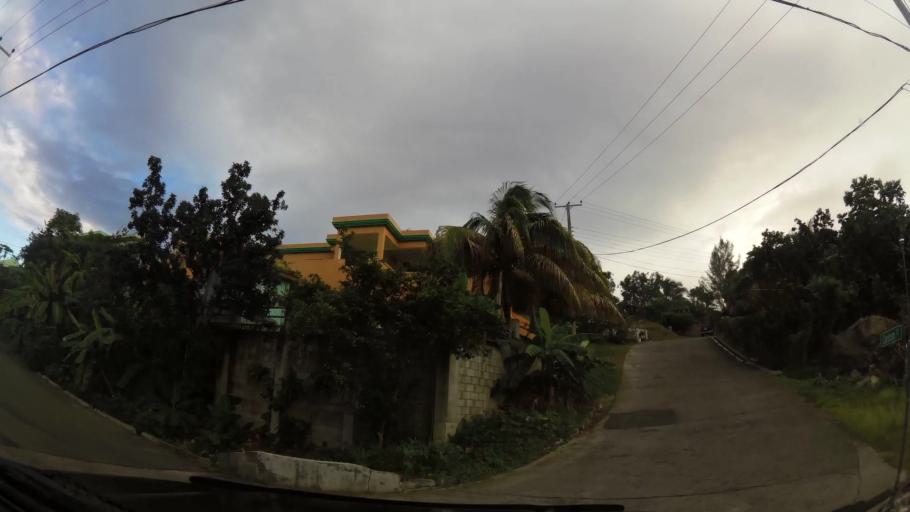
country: MS
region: Saint Peter
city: Brades
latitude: 16.7936
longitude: -62.1865
